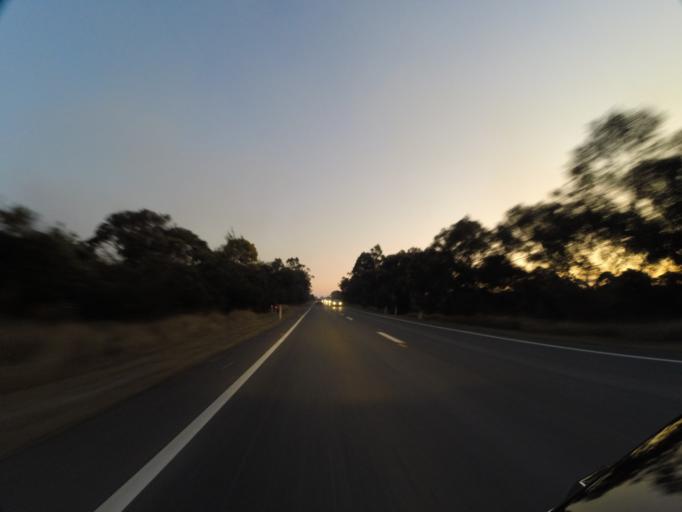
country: AU
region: New South Wales
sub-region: Sutherland Shire
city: Menai
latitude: -34.0050
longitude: 150.9922
